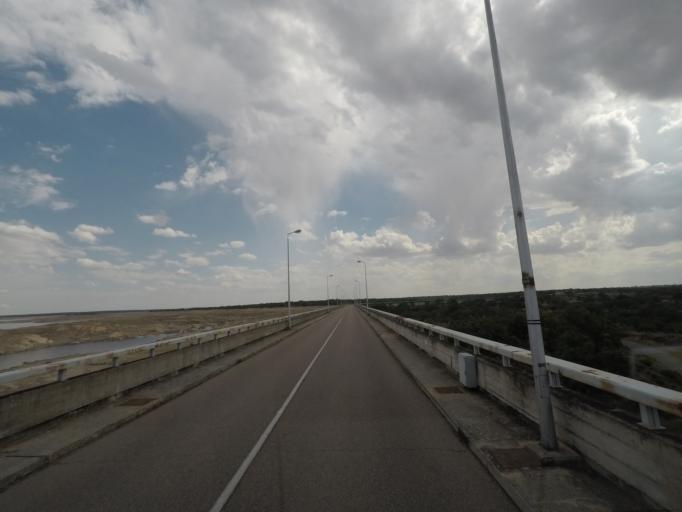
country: ES
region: Castille and Leon
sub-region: Provincia de Salamanca
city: Almendra
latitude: 41.2643
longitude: -6.3231
